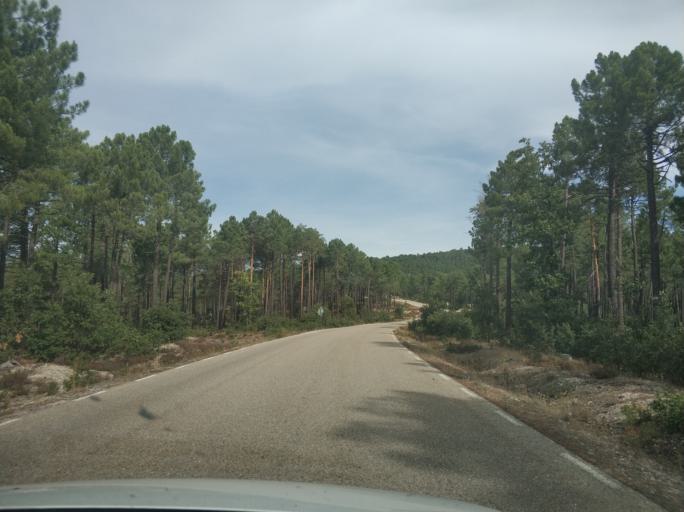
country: ES
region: Castille and Leon
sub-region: Provincia de Soria
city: Duruelo de la Sierra
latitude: 41.8834
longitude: -2.9374
